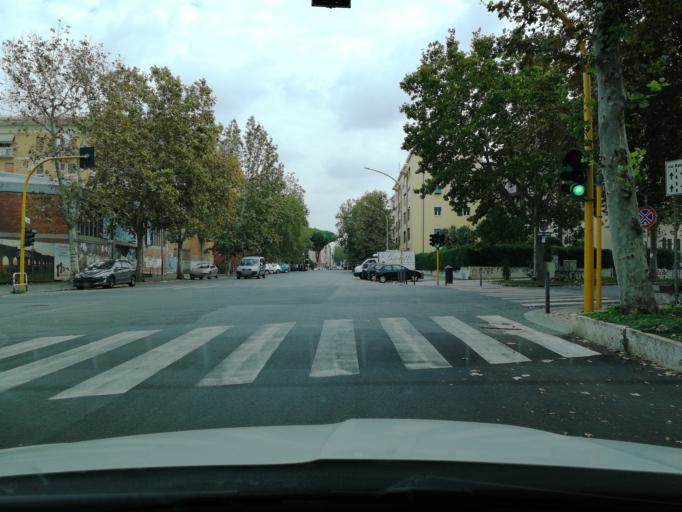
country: IT
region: Latium
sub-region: Citta metropolitana di Roma Capitale
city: Rome
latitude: 41.8588
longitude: 12.5536
